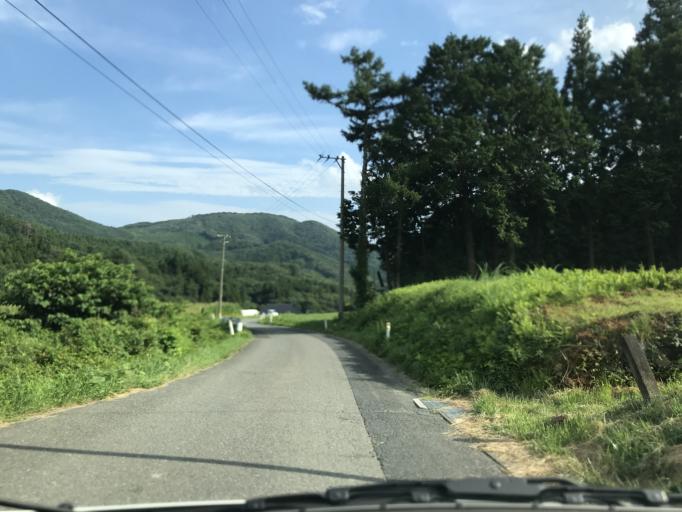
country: JP
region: Iwate
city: Ofunato
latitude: 38.9654
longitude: 141.4718
